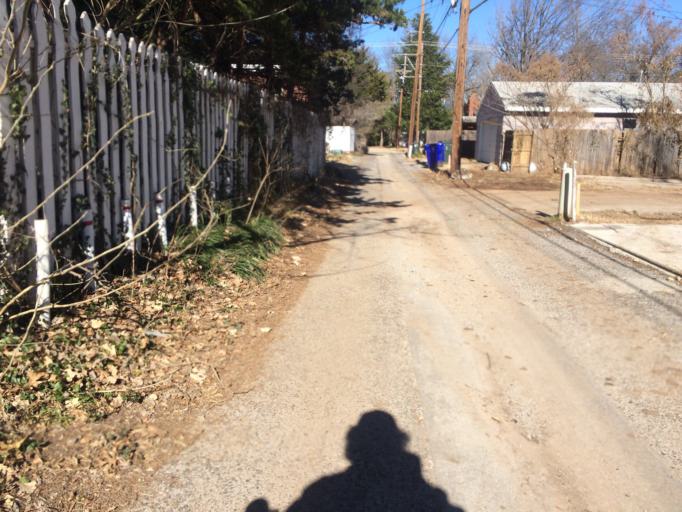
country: US
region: Oklahoma
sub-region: Cleveland County
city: Norman
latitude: 35.2068
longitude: -97.4523
